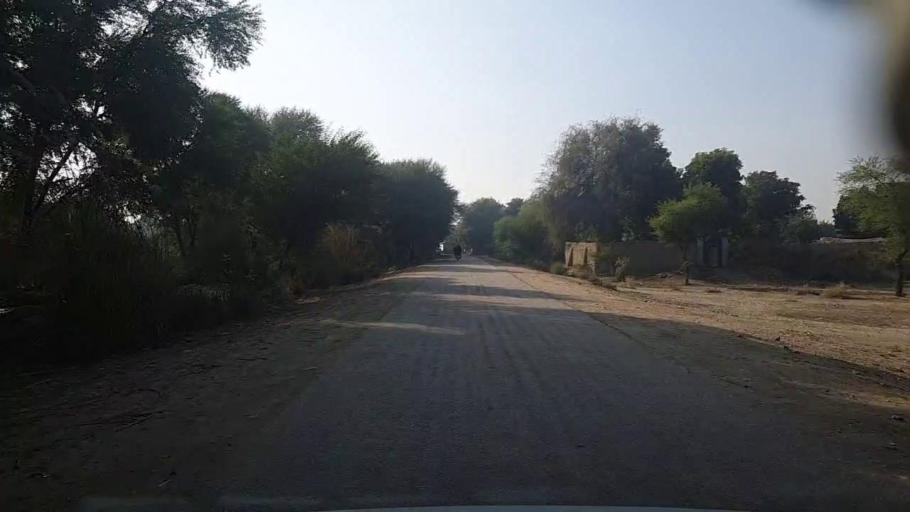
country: PK
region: Sindh
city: Kandiari
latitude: 26.8458
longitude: 68.4917
